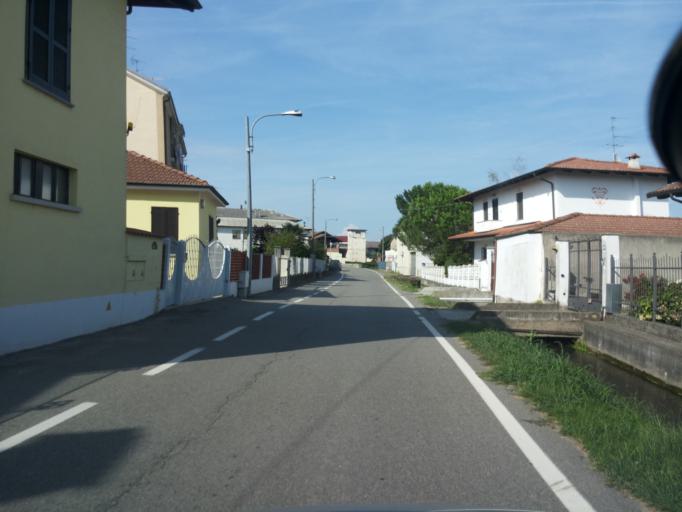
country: IT
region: Piedmont
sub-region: Provincia di Vercelli
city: San Germano Vercellese
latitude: 45.3486
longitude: 8.2458
